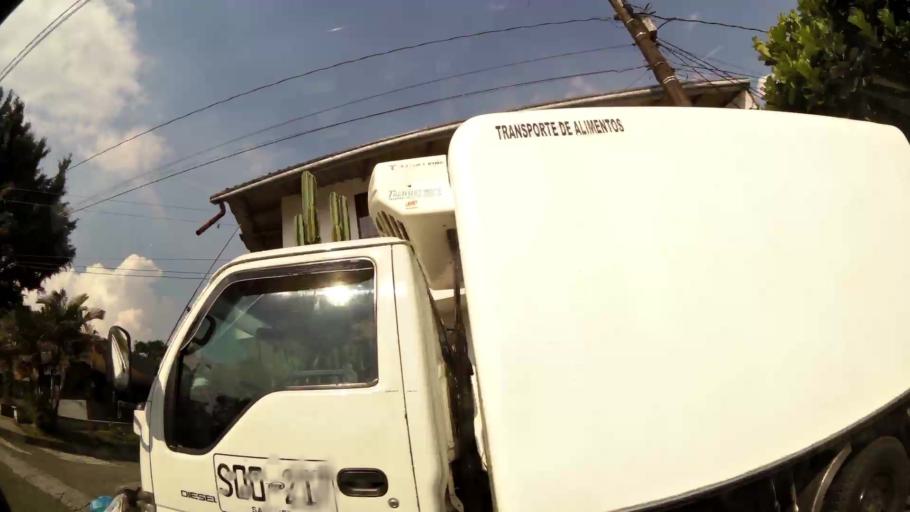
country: CO
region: Antioquia
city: Medellin
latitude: 6.2909
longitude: -75.5925
